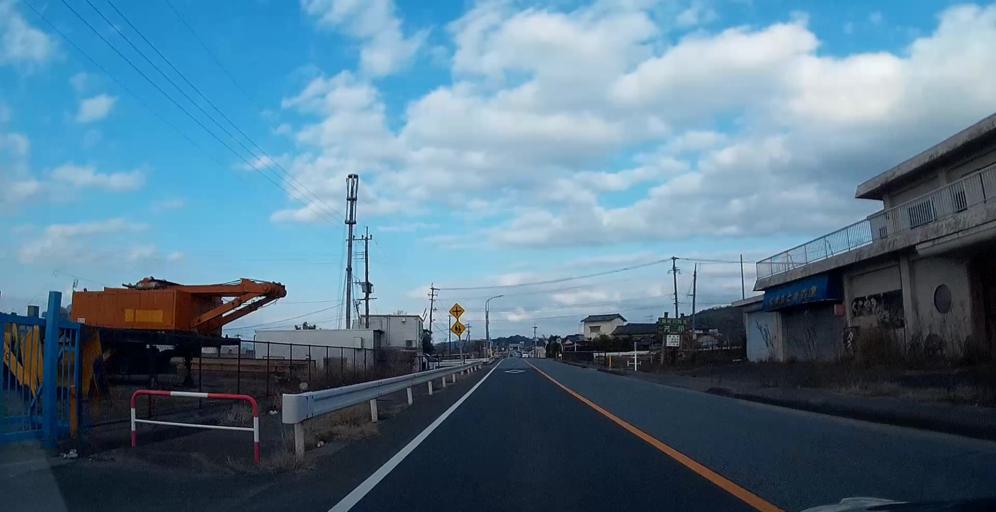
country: JP
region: Kumamoto
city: Yatsushiro
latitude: 32.5323
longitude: 130.6650
